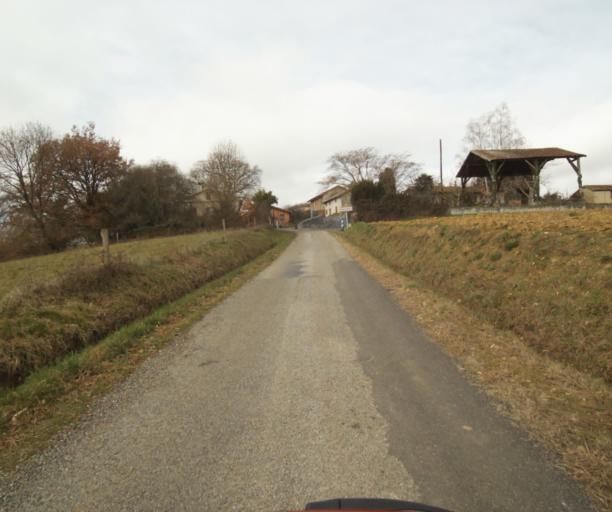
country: FR
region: Midi-Pyrenees
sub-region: Departement de l'Ariege
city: Pamiers
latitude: 43.1051
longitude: 1.5171
